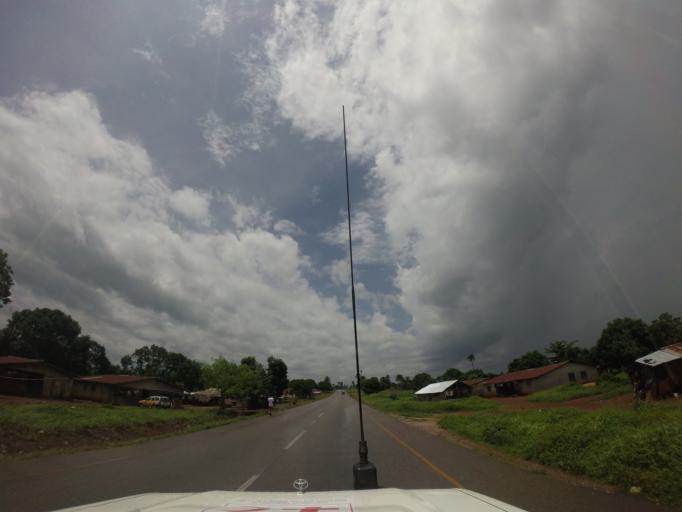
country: SL
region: Southern Province
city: Rotifunk
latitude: 8.4887
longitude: -12.7482
